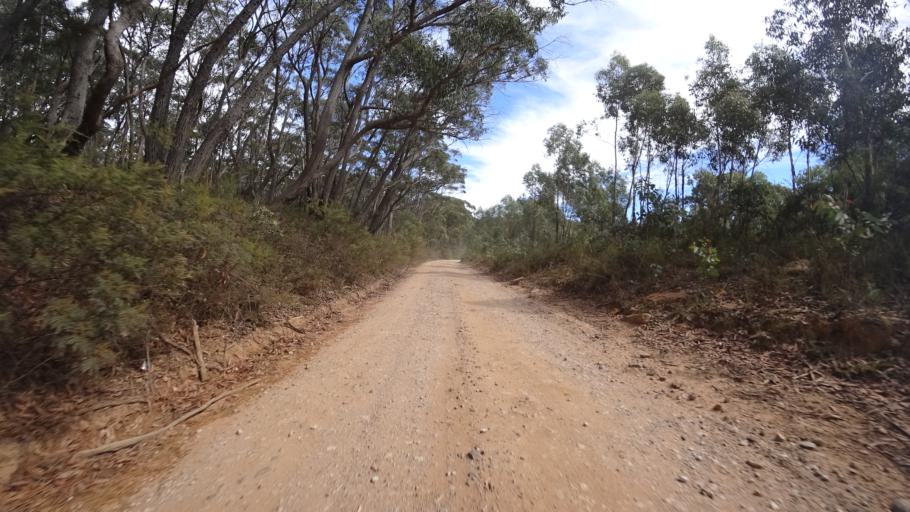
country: AU
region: New South Wales
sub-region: Lithgow
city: Lithgow
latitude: -33.3398
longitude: 150.2507
